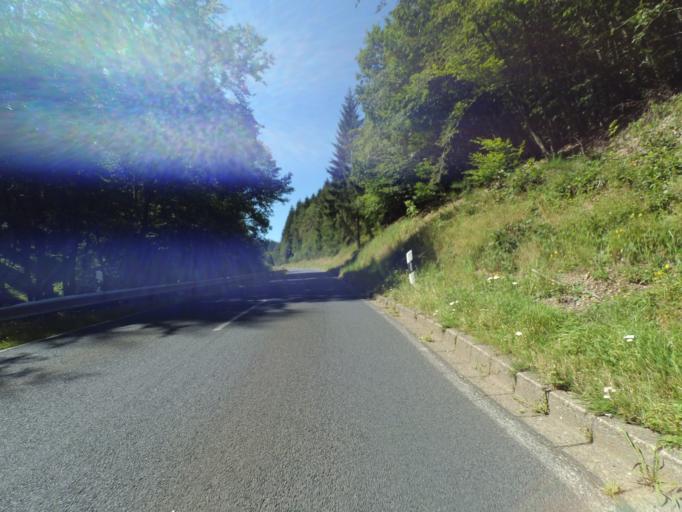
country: DE
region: Rheinland-Pfalz
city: Weidenbach
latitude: 50.1273
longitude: 6.7304
